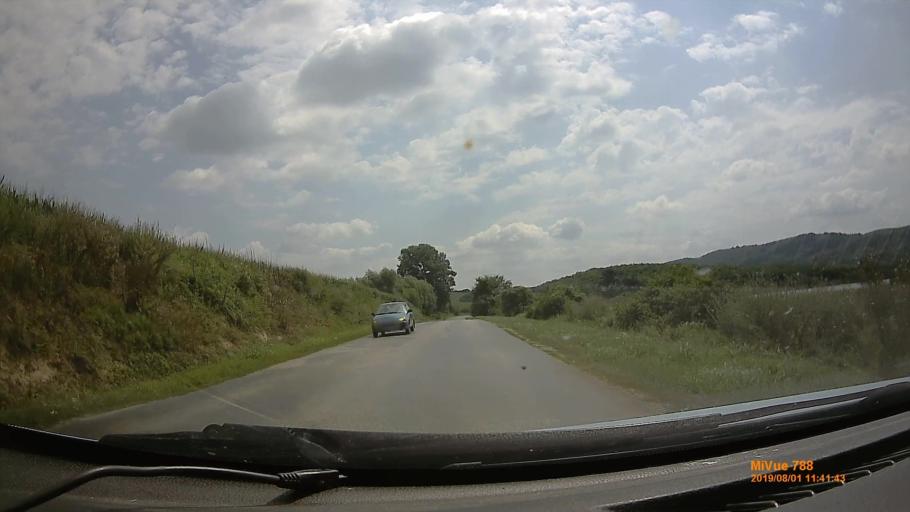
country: HU
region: Baranya
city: Villany
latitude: 45.8901
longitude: 18.4073
